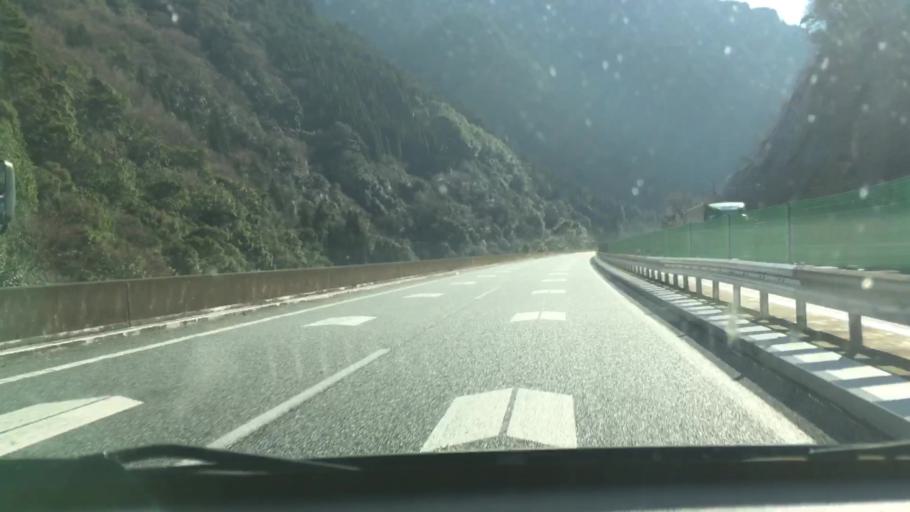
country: JP
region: Kumamoto
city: Hitoyoshi
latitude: 32.3225
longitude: 130.7580
